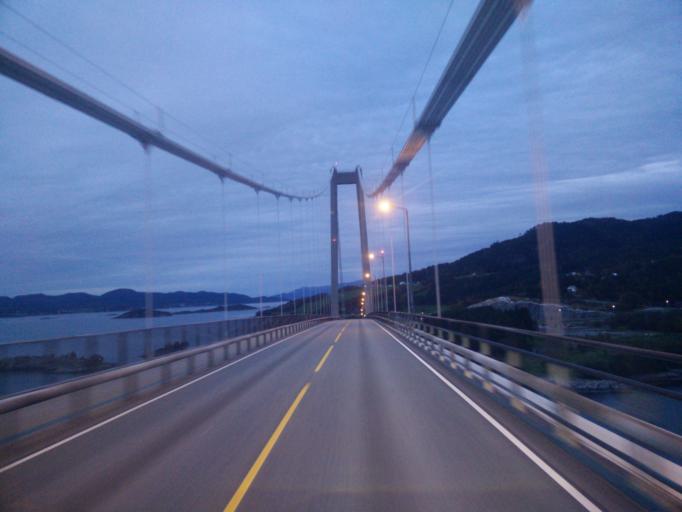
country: NO
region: More og Romsdal
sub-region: Gjemnes
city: Batnfjordsora
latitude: 62.9717
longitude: 7.7800
